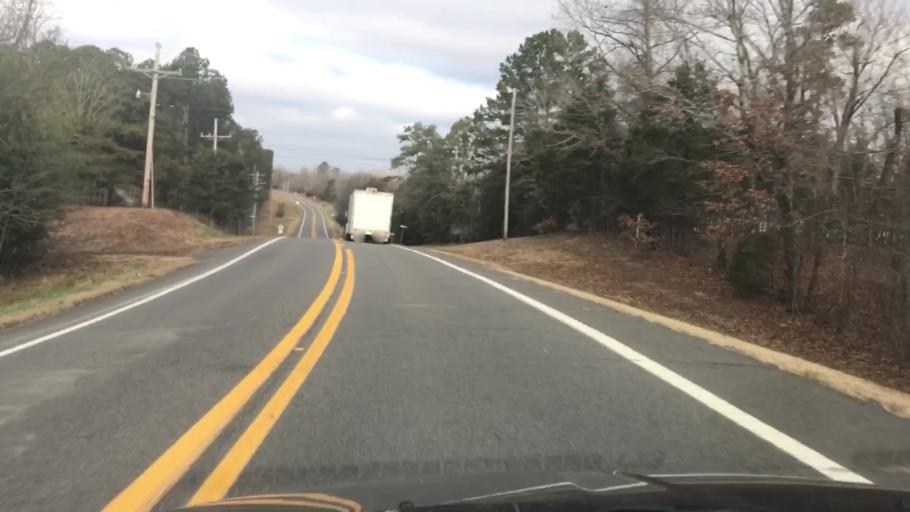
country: US
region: Arkansas
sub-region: Montgomery County
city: Mount Ida
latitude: 34.6213
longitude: -93.7234
